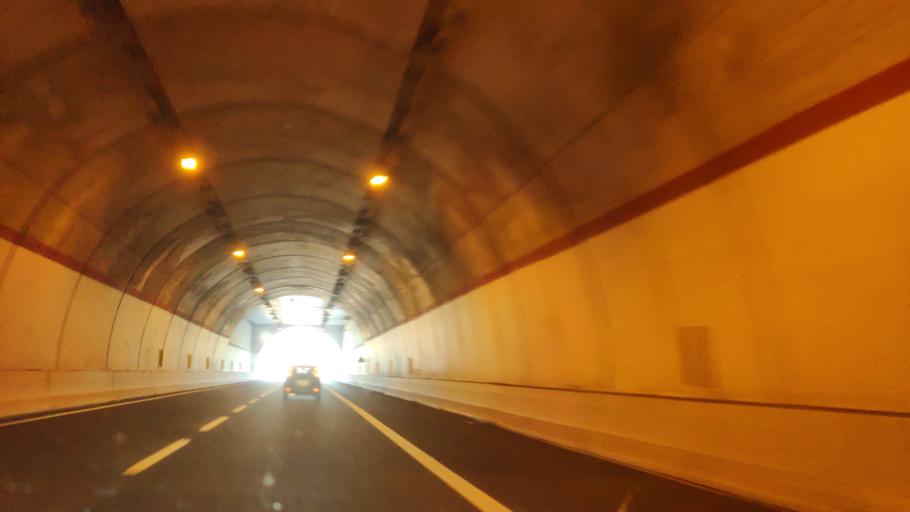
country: IT
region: Basilicate
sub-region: Provincia di Potenza
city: Lauria
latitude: 40.0229
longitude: 15.8792
